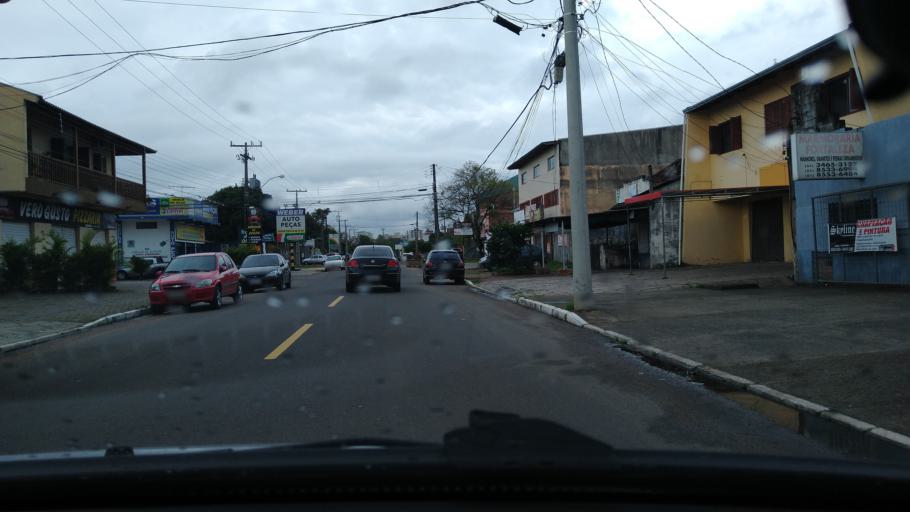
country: BR
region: Rio Grande do Sul
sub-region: Canoas
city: Canoas
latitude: -29.9184
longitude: -51.1948
